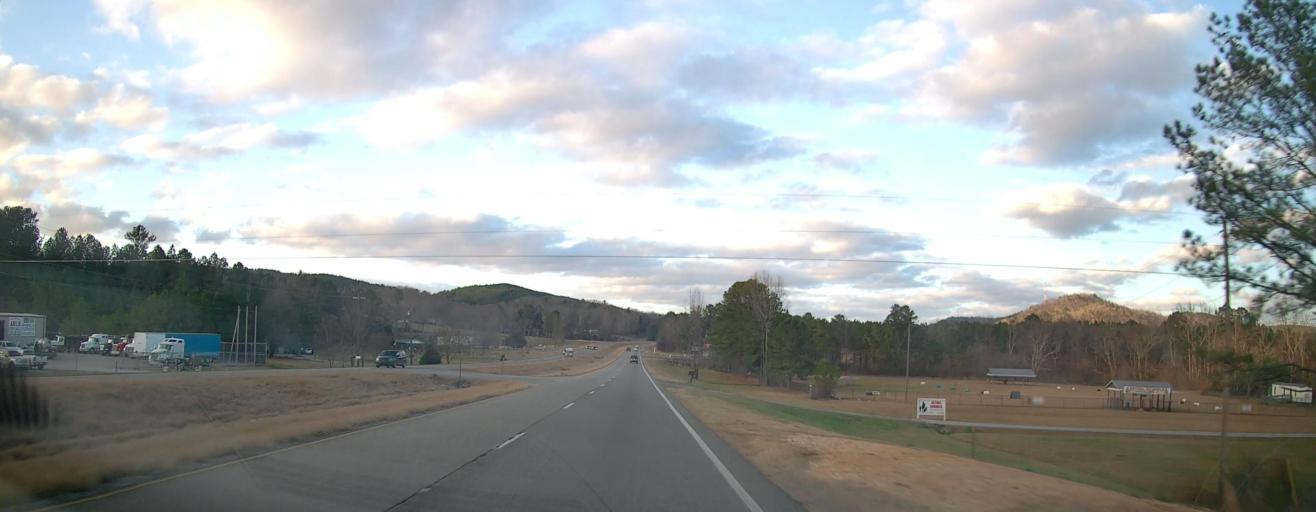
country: US
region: Alabama
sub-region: Etowah County
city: Glencoe
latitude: 33.9103
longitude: -85.9118
